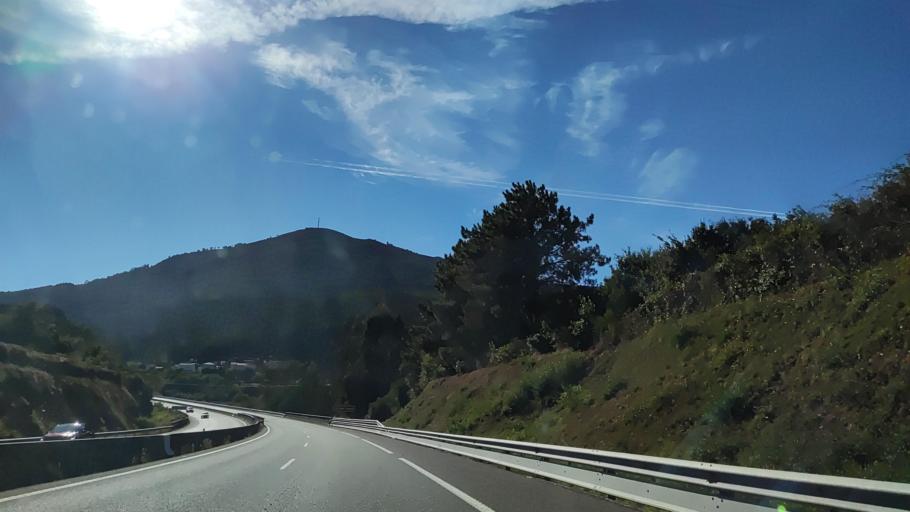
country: ES
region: Galicia
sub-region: Provincia da Coruna
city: Boiro
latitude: 42.6235
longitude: -8.9386
